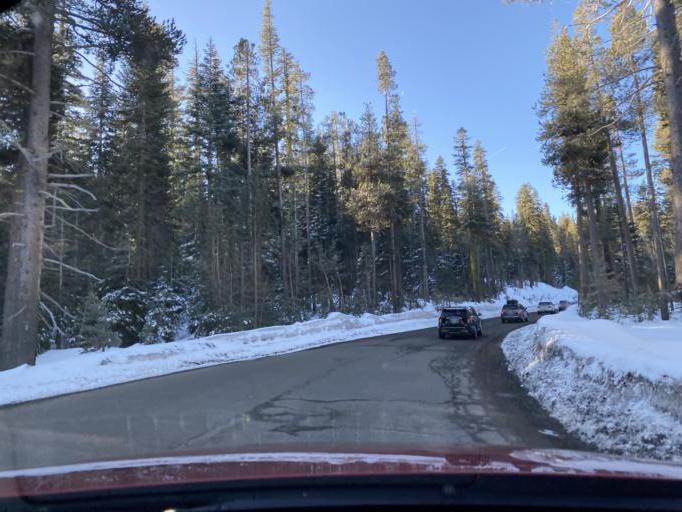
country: US
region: California
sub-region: El Dorado County
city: South Lake Tahoe
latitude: 38.8171
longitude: -120.0739
